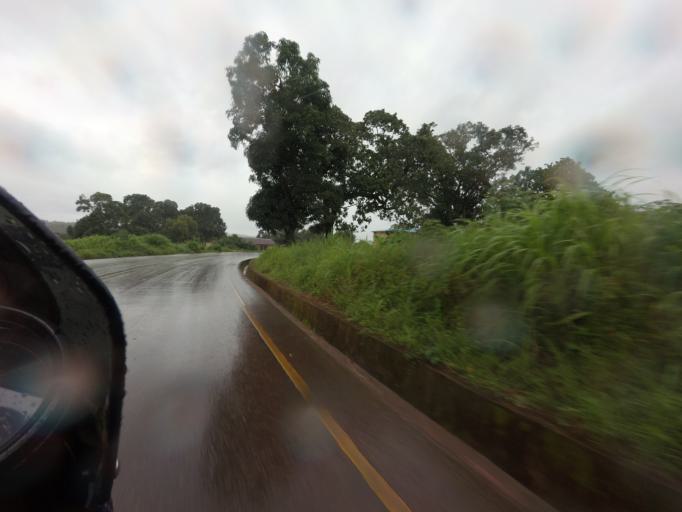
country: SL
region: Northern Province
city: Kambia
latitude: 9.1165
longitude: -12.9233
